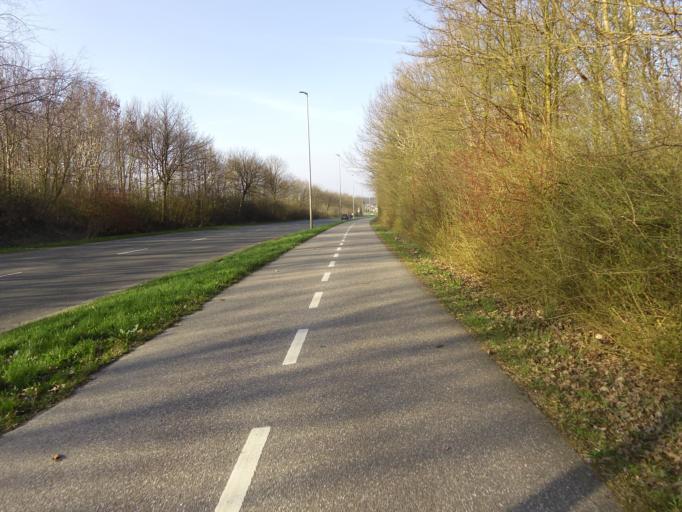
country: DK
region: South Denmark
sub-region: Vejen Kommune
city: Vejen
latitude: 55.4856
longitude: 9.1264
